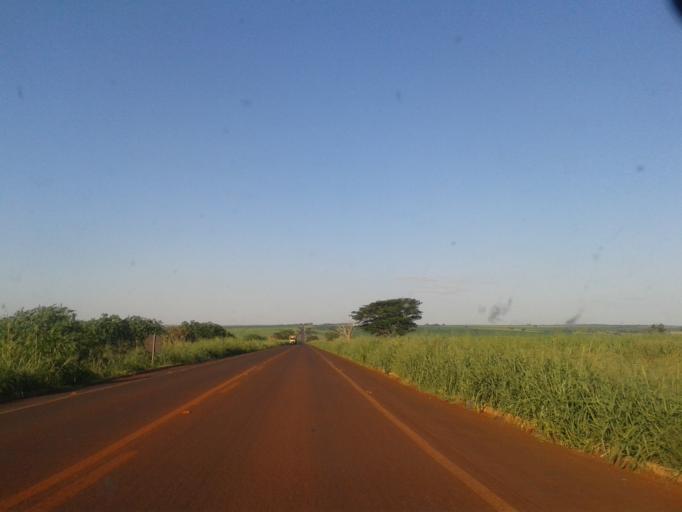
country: BR
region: Minas Gerais
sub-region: Capinopolis
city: Capinopolis
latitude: -18.7047
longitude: -49.6823
